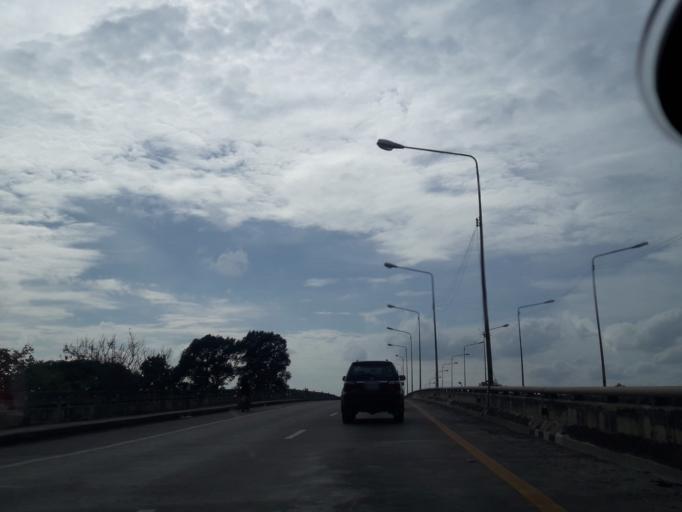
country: TH
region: Sara Buri
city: Saraburi
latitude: 14.5566
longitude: 100.9255
